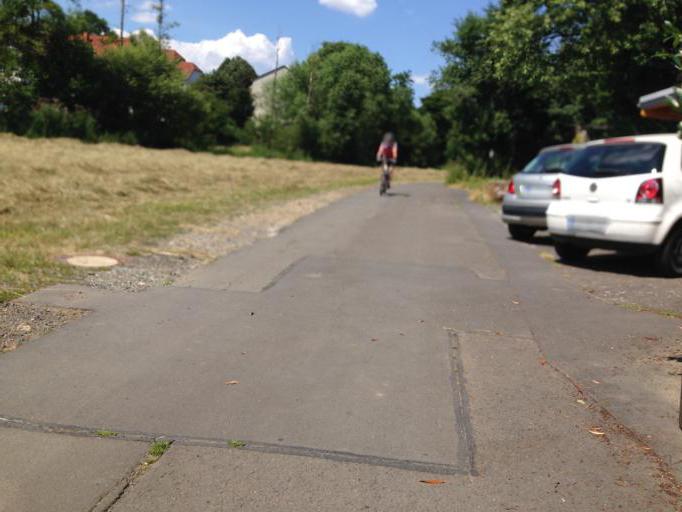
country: DE
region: Hesse
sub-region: Regierungsbezirk Giessen
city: Heuchelheim
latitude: 50.6164
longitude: 8.6446
